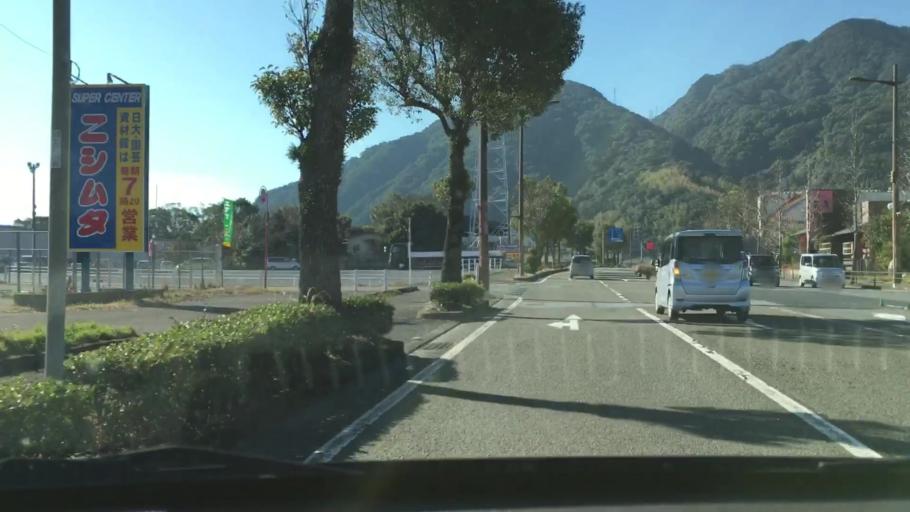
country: JP
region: Kagoshima
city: Kajiki
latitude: 31.7082
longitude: 130.6149
